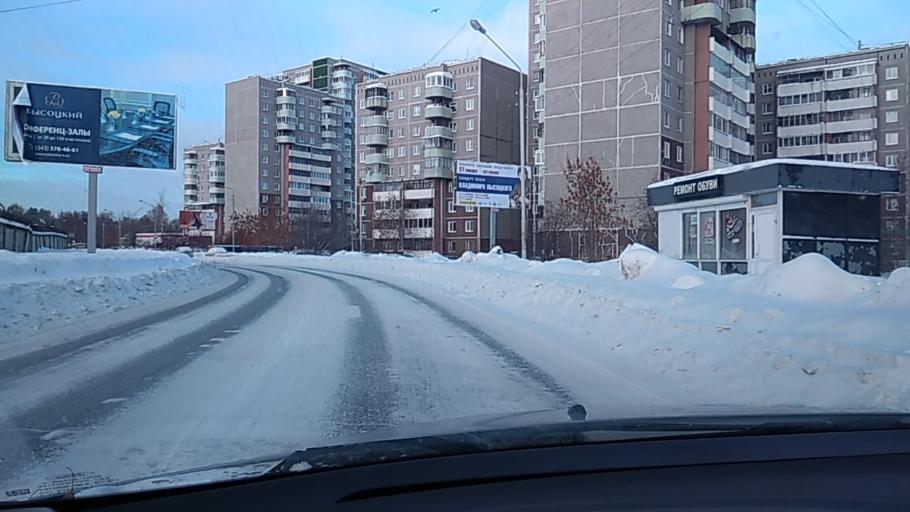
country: RU
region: Sverdlovsk
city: Yekaterinburg
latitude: 56.7920
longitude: 60.6113
